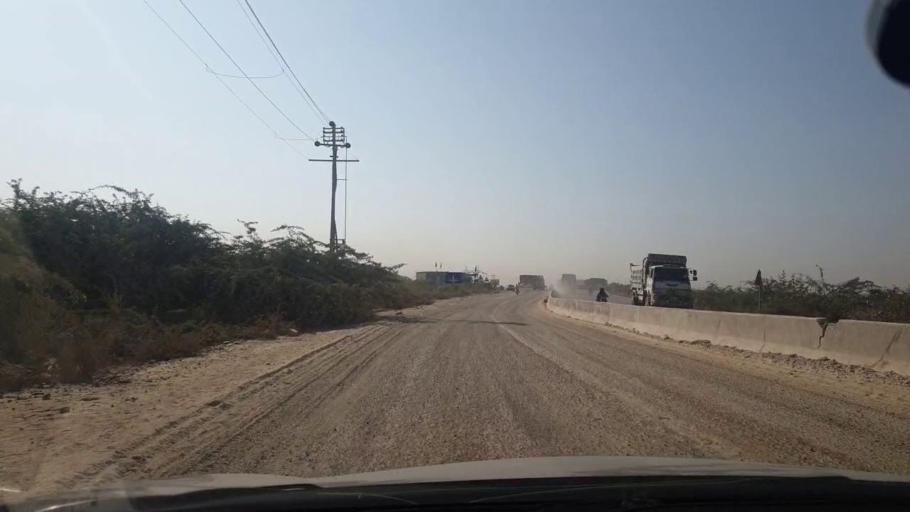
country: PK
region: Sindh
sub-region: Karachi District
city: Karachi
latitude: 25.0764
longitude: 67.0139
